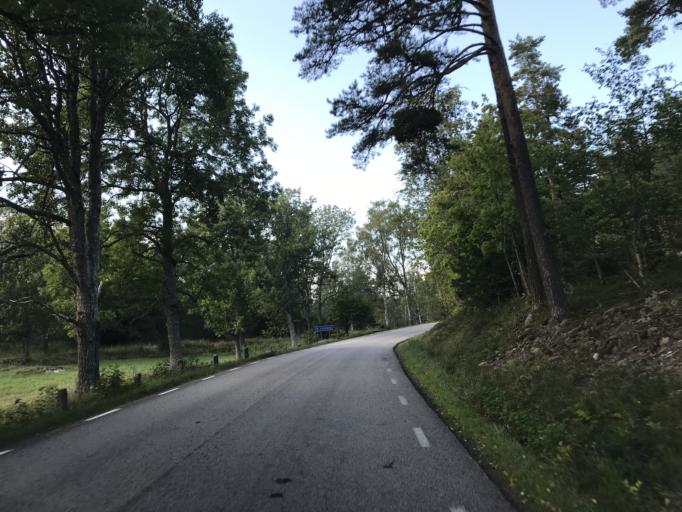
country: SE
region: Stockholm
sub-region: Norrtalje Kommun
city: Bjorko
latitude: 59.8707
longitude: 19.0129
